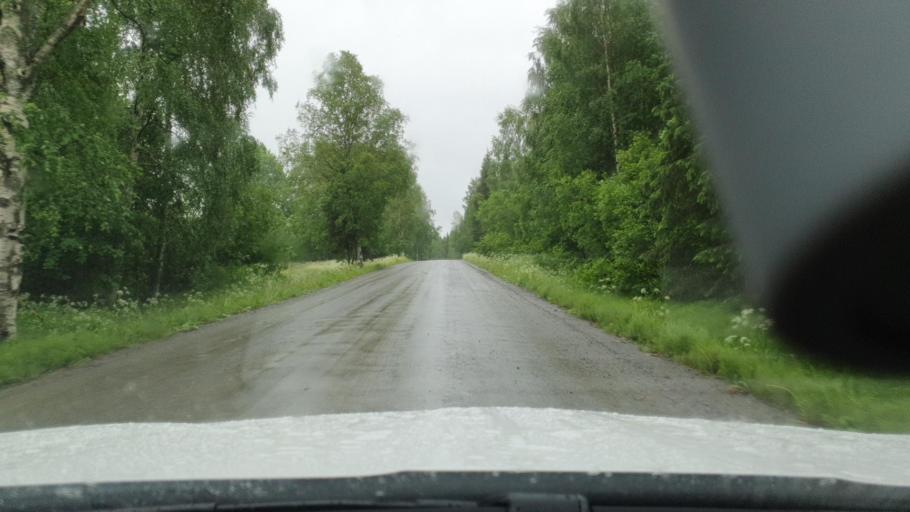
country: SE
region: Vaesterbotten
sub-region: Skelleftea Kommun
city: Burtraesk
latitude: 64.3517
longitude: 20.4820
